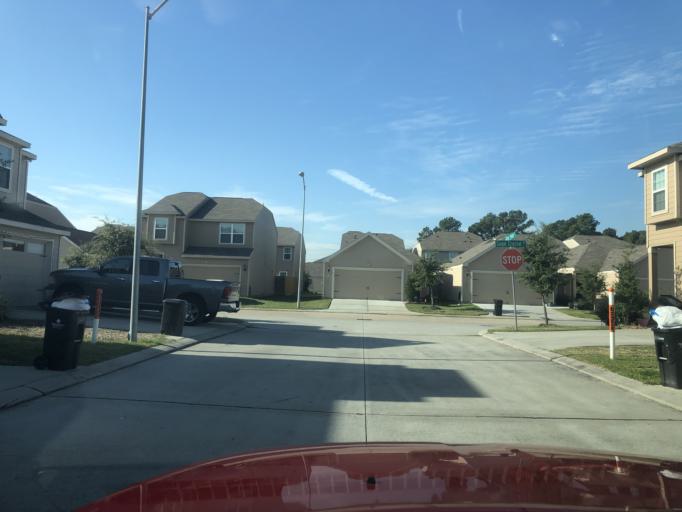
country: US
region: Texas
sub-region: Harris County
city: Spring
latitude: 30.0112
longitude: -95.4608
